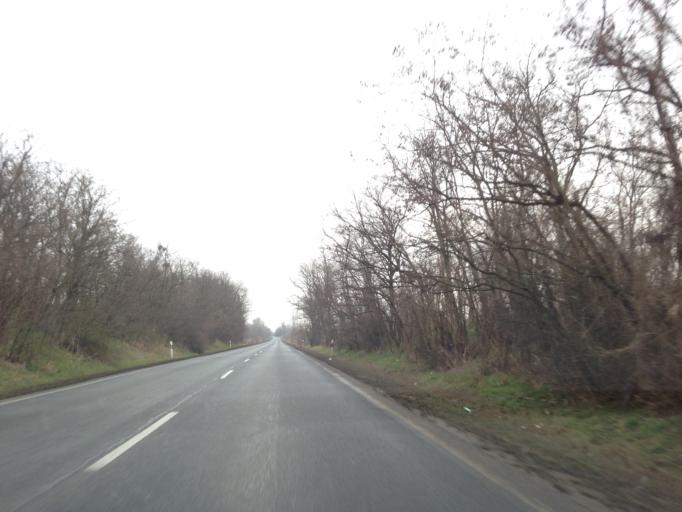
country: HU
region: Komarom-Esztergom
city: Szomod
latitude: 47.6912
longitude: 18.3096
